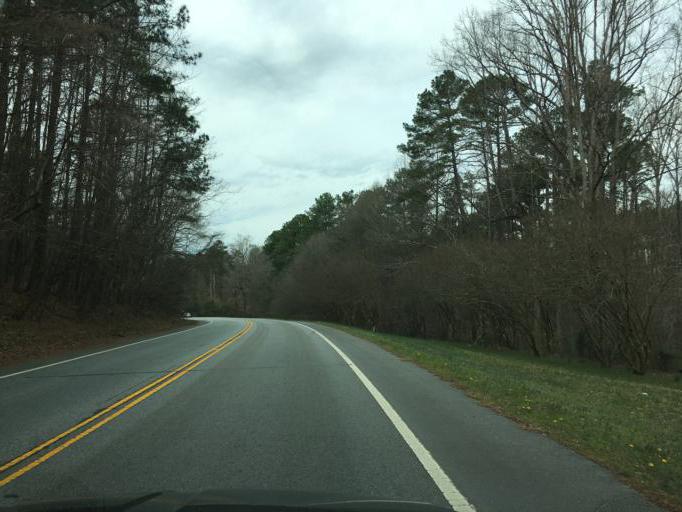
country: US
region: South Carolina
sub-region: Anderson County
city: Pendleton
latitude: 34.6624
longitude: -82.7920
